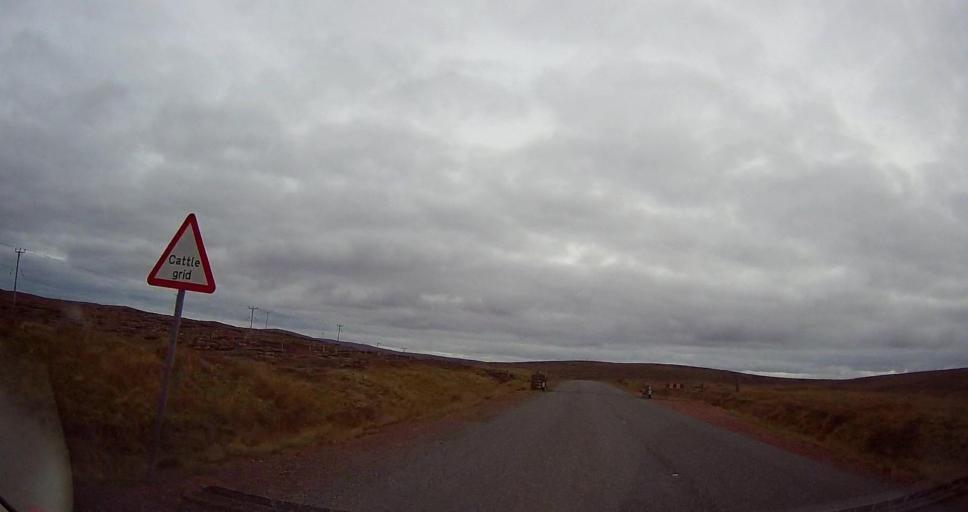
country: GB
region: Scotland
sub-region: Shetland Islands
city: Shetland
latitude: 60.6280
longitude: -1.0697
